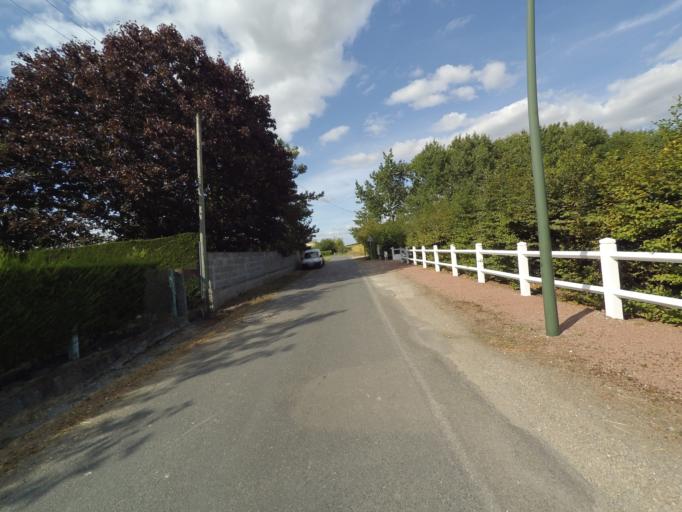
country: FR
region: Pays de la Loire
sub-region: Departement de la Loire-Atlantique
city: Vieillevigne
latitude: 46.9702
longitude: -1.4238
